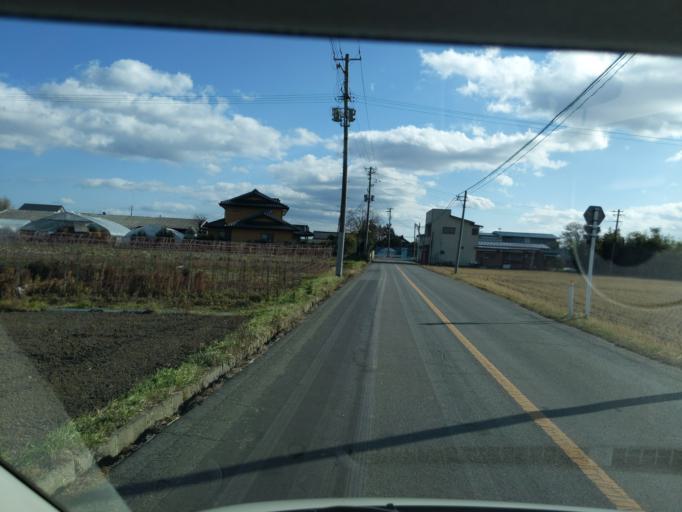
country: JP
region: Miyagi
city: Kogota
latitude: 38.7166
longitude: 141.0797
